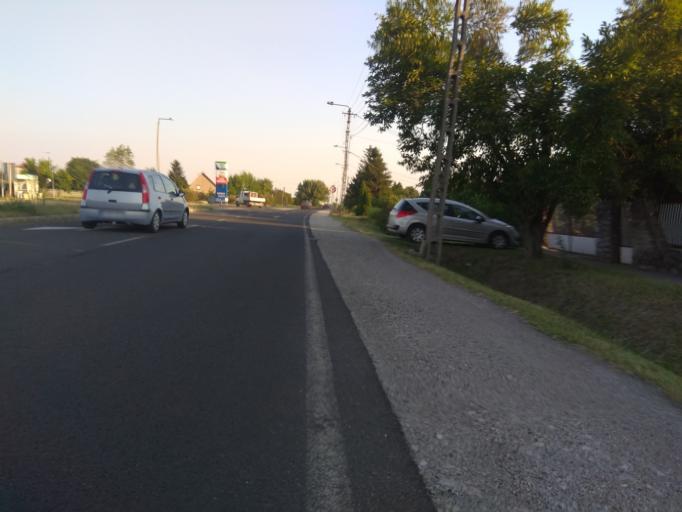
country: HU
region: Borsod-Abauj-Zemplen
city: Nyekladhaza
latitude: 47.9868
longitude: 20.8311
